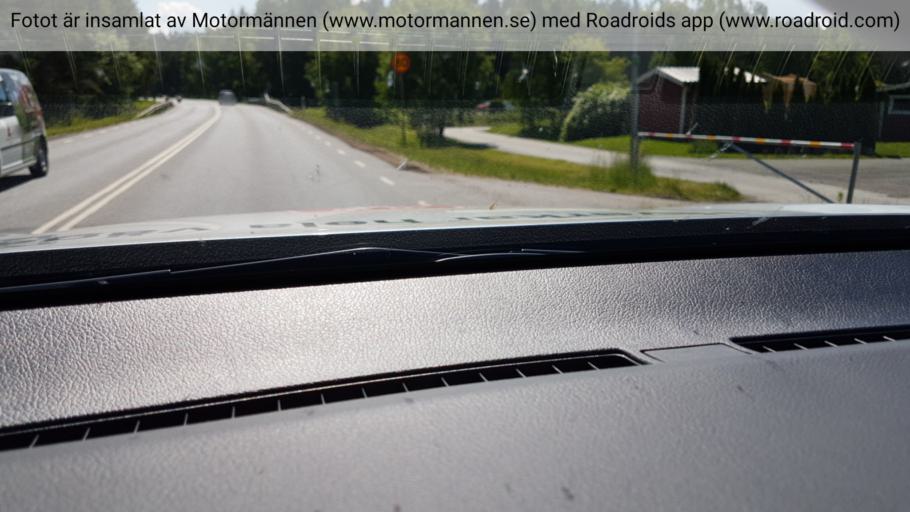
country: SE
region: Vaestra Goetaland
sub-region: Lidkopings Kommun
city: Lidkoping
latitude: 58.4988
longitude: 13.1298
